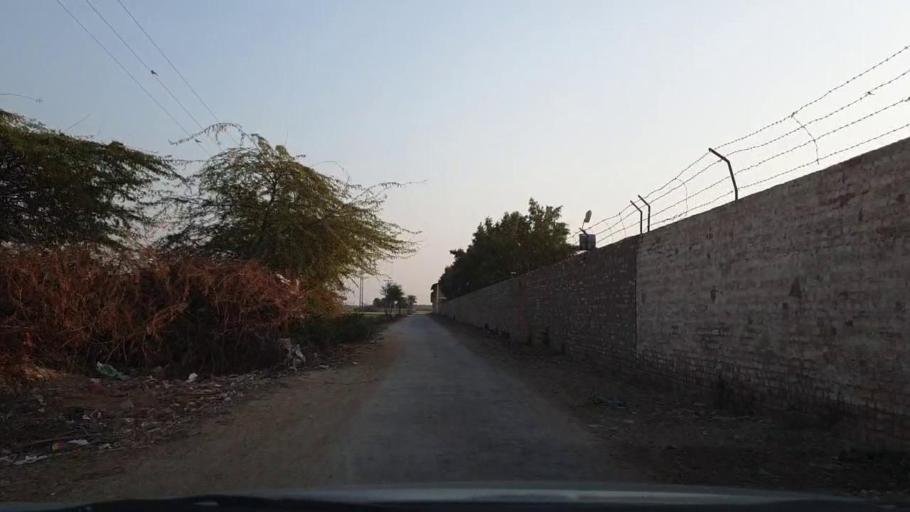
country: PK
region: Sindh
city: Tando Adam
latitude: 25.7199
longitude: 68.5932
